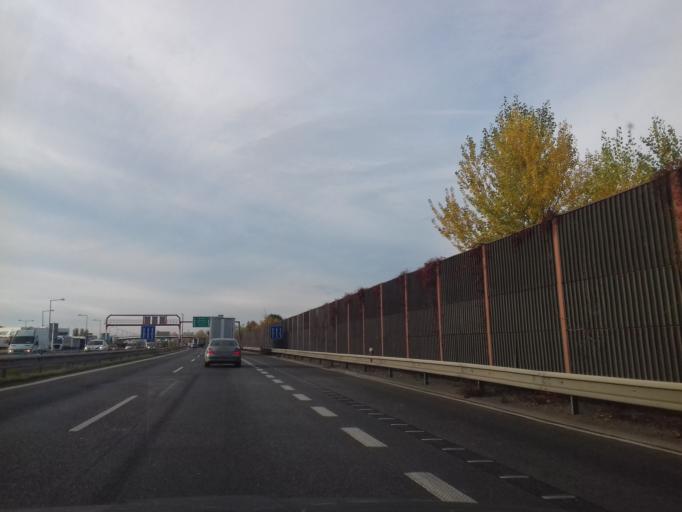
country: SK
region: Bratislavsky
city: Svaty Jur
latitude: 48.1798
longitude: 17.1931
